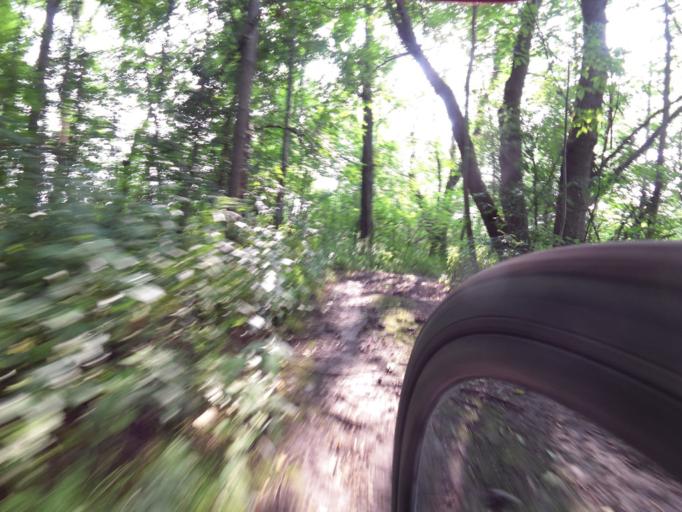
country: CA
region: Ontario
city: Quinte West
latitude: 44.0465
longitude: -77.6279
